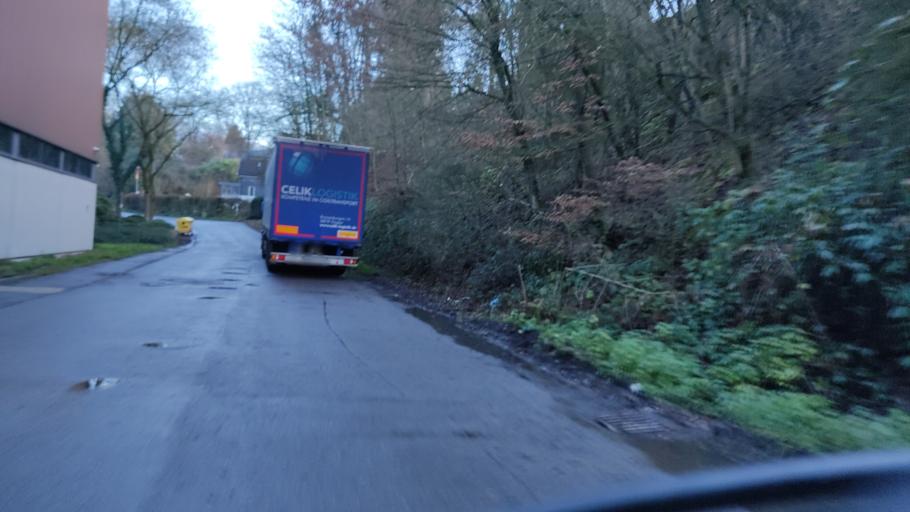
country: DE
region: North Rhine-Westphalia
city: Hattingen
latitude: 51.3737
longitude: 7.1286
